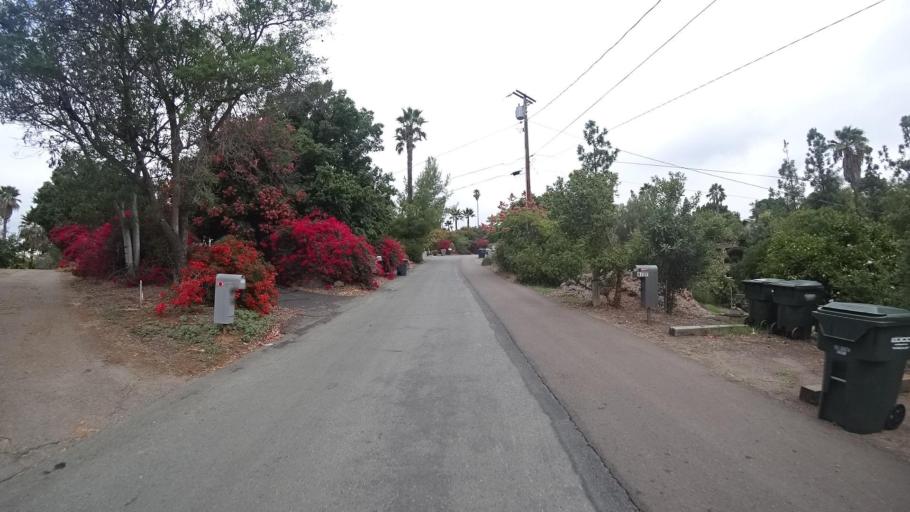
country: US
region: California
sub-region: San Diego County
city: Spring Valley
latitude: 32.7534
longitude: -116.9914
